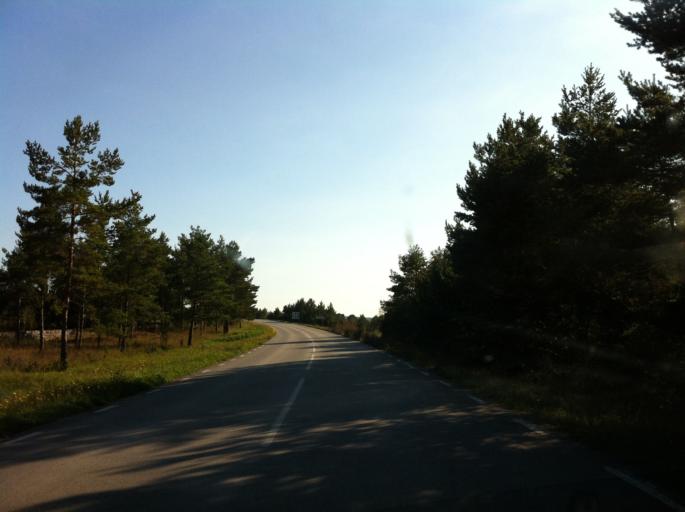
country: SE
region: Gotland
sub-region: Gotland
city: Slite
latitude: 57.8748
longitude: 19.0851
